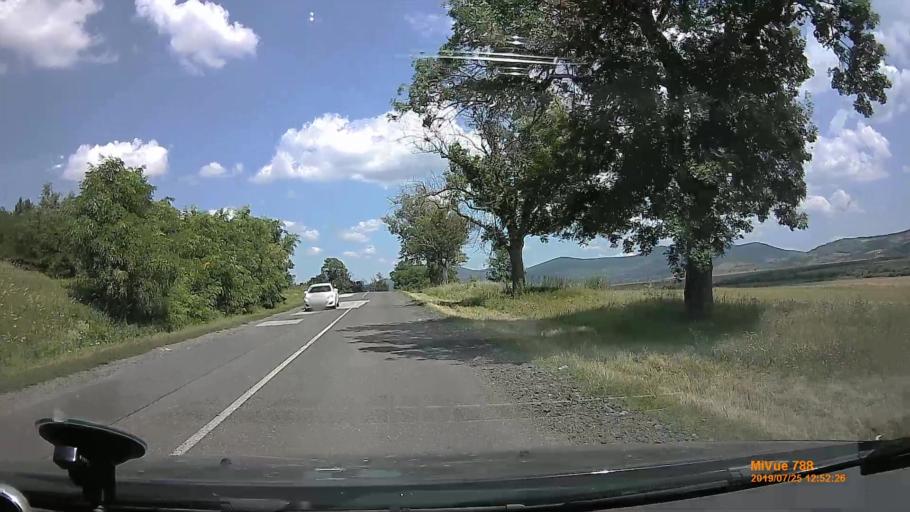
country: HU
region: Borsod-Abauj-Zemplen
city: Abaujszanto
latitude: 48.2912
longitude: 21.1882
